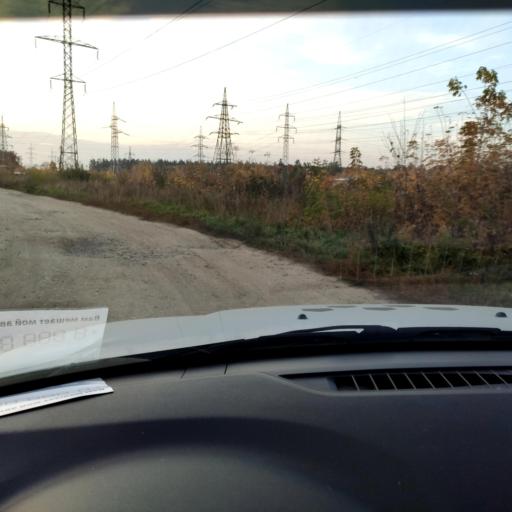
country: RU
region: Samara
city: Zhigulevsk
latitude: 53.5176
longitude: 49.4737
